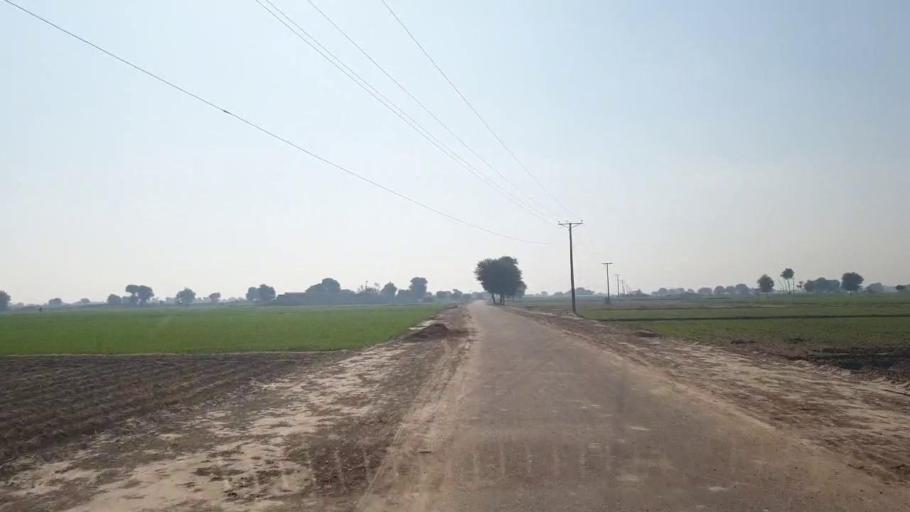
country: PK
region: Sindh
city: Shahpur Chakar
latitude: 26.1048
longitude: 68.6007
